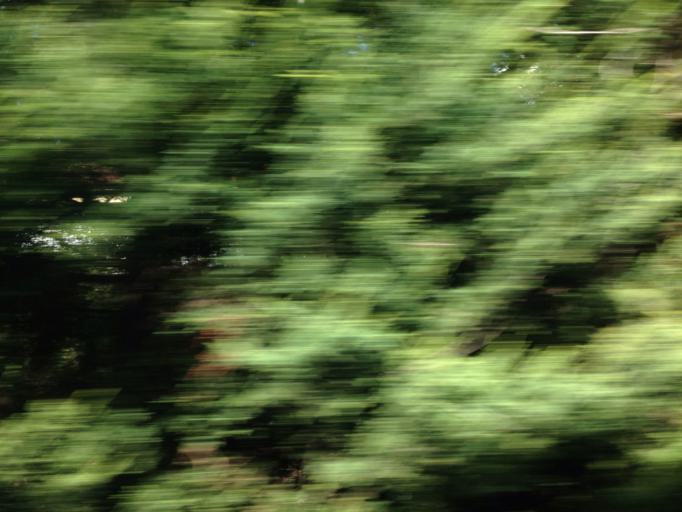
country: AU
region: New South Wales
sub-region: North Sydney
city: Wollstonecraft
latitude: -33.8294
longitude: 151.1946
